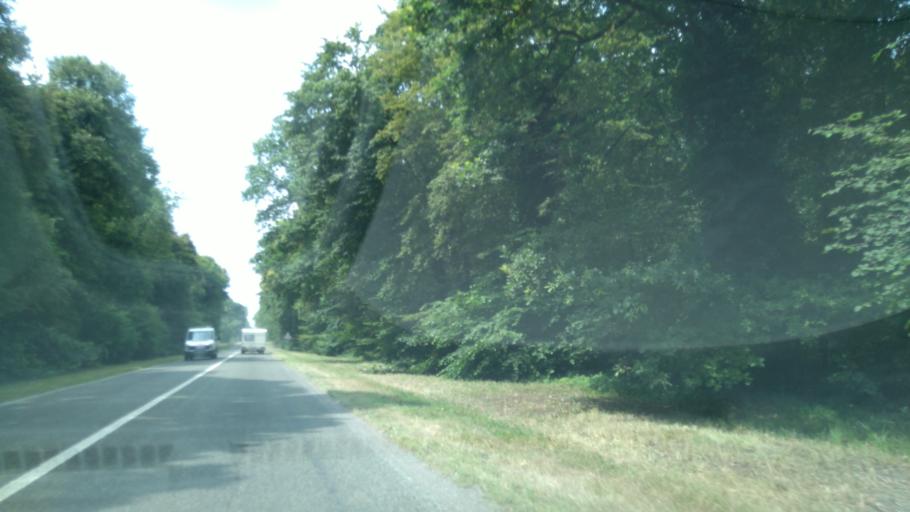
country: FR
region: Picardie
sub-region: Departement de l'Oise
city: Chantilly
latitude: 49.2065
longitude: 2.4599
